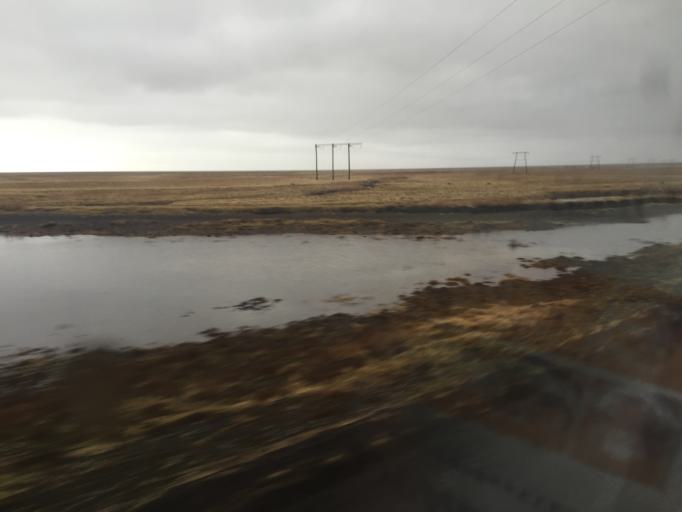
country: IS
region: East
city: Hoefn
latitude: 63.8844
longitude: -16.6915
